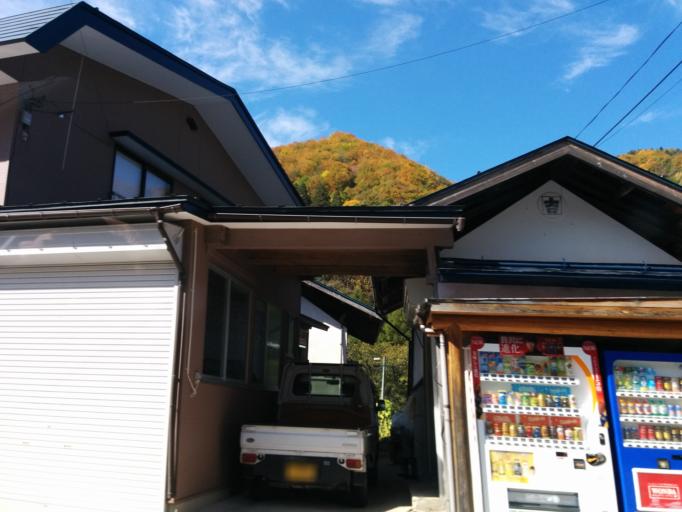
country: JP
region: Tochigi
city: Nikko
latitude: 37.1101
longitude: 139.4541
